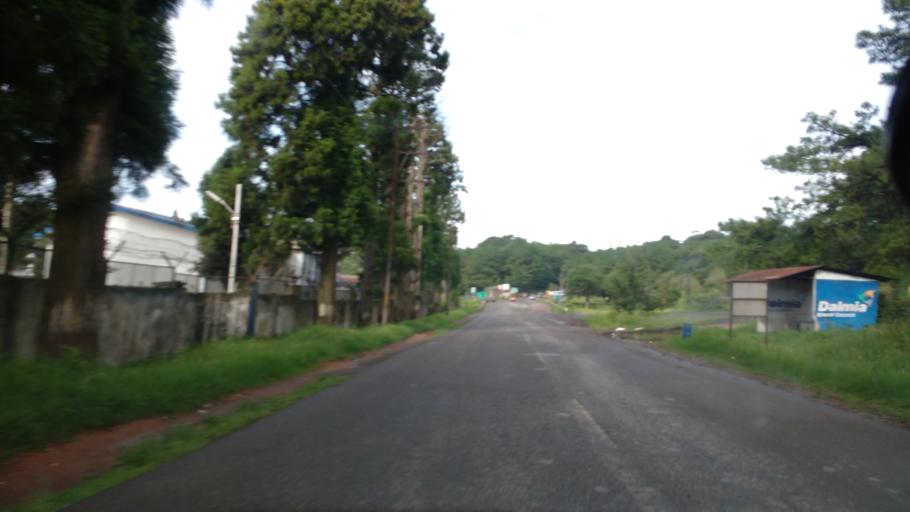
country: IN
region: Meghalaya
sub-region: East Khasi Hills
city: Shillong
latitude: 25.5362
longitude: 91.8260
